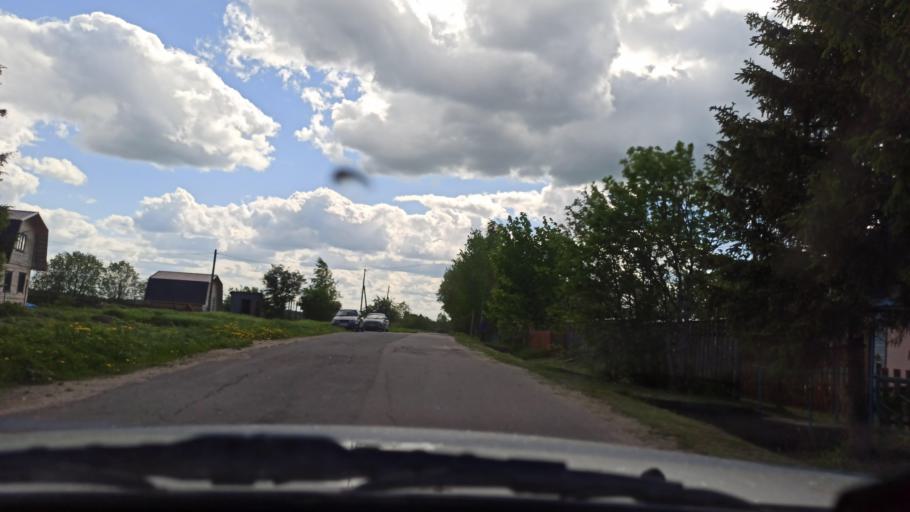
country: RU
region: Vologda
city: Molochnoye
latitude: 59.3781
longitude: 39.7170
